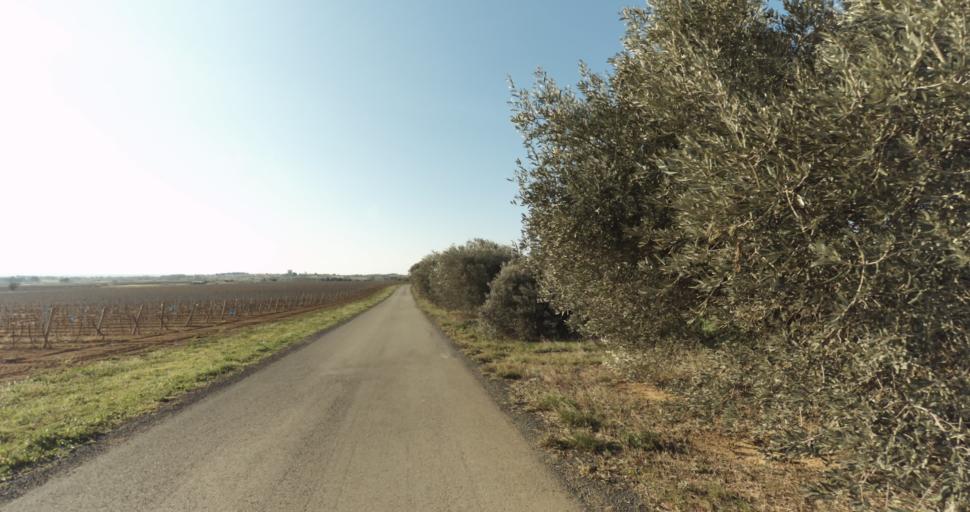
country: FR
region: Languedoc-Roussillon
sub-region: Departement de l'Herault
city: Pomerols
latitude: 43.3799
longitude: 3.5184
